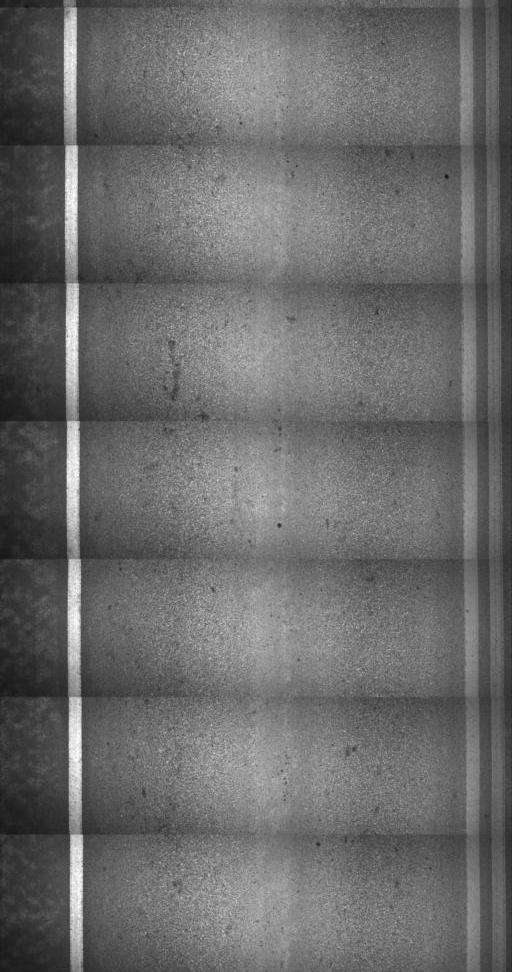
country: US
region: Vermont
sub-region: Franklin County
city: Swanton
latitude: 44.9222
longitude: -72.9662
